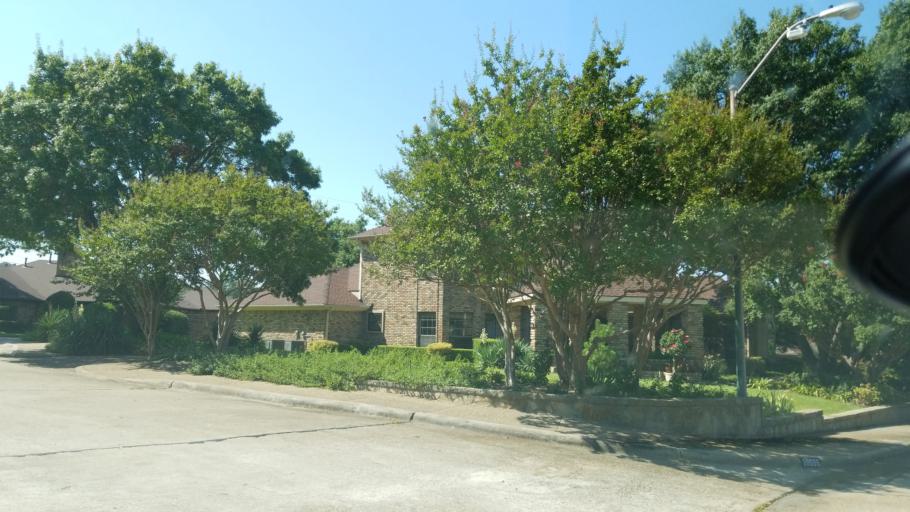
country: US
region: Texas
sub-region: Dallas County
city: Richardson
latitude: 32.9100
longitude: -96.7129
